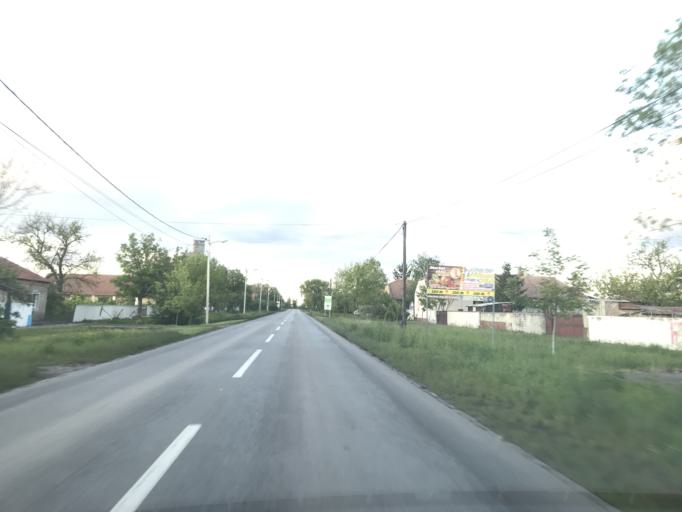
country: RS
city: Cestereg
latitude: 45.5662
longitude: 20.5360
